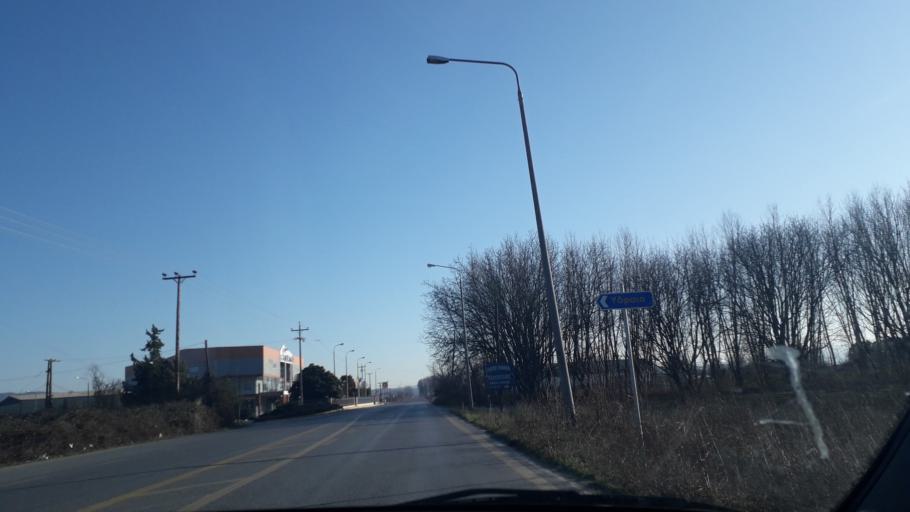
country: GR
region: Central Macedonia
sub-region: Nomos Pellis
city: Aridaia
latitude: 40.9642
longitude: 22.0693
